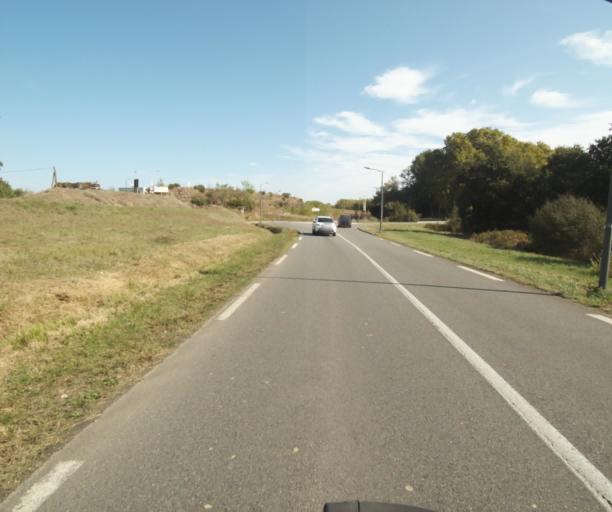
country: FR
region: Midi-Pyrenees
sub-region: Departement du Tarn-et-Garonne
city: Verdun-sur-Garonne
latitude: 43.8561
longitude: 1.2188
